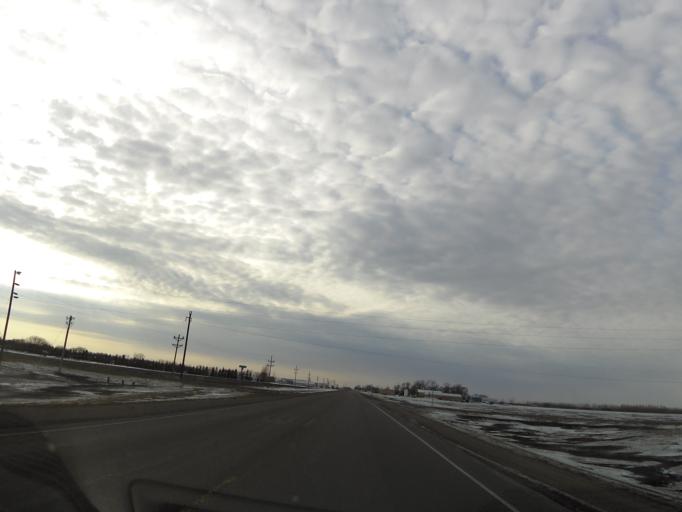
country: US
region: North Dakota
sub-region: Walsh County
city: Grafton
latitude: 48.5714
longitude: -97.1673
